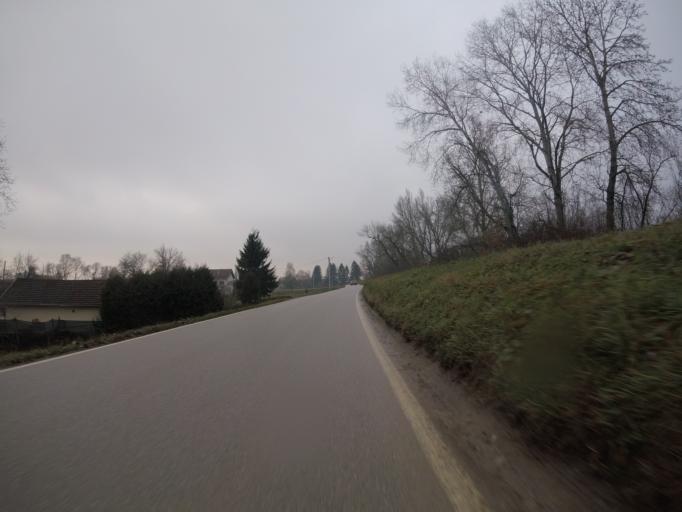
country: HR
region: Zagrebacka
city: Kuce
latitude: 45.7007
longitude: 16.2122
